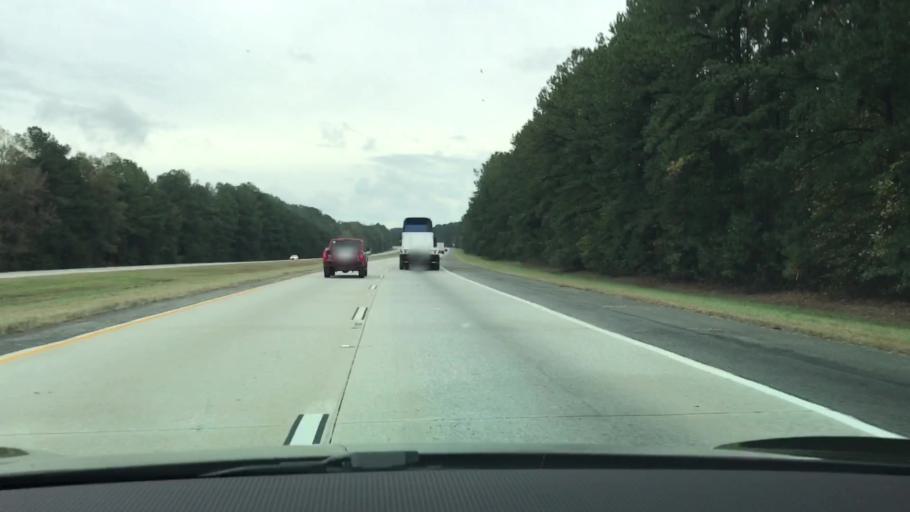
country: US
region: Georgia
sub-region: Taliaferro County
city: Crawfordville
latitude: 33.5370
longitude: -82.9975
